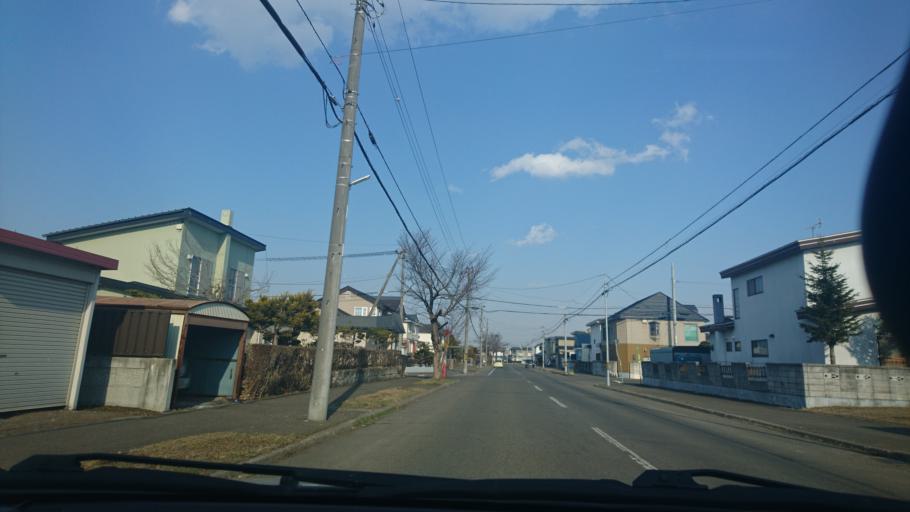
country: JP
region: Hokkaido
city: Obihiro
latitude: 42.9210
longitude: 143.1548
